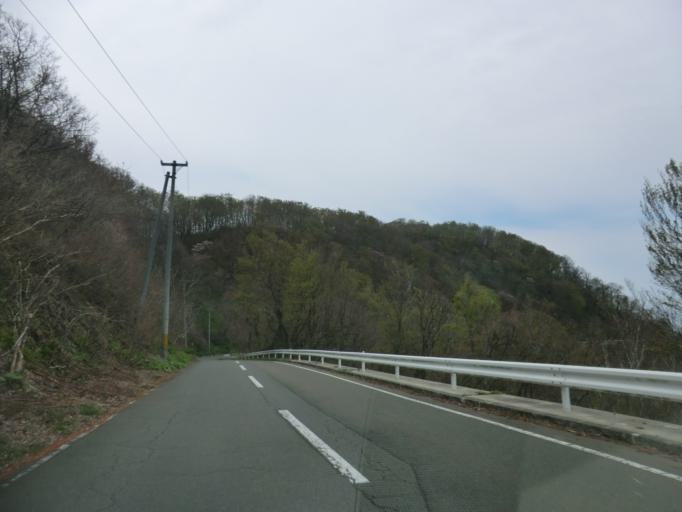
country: JP
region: Aomori
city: Mutsu
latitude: 41.3224
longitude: 140.8106
